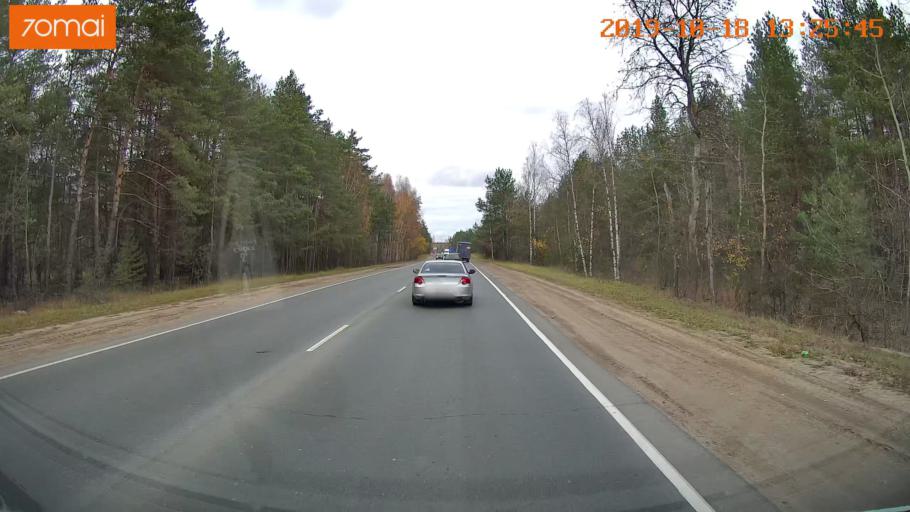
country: RU
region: Rjazan
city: Polyany
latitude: 54.7460
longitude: 39.8402
